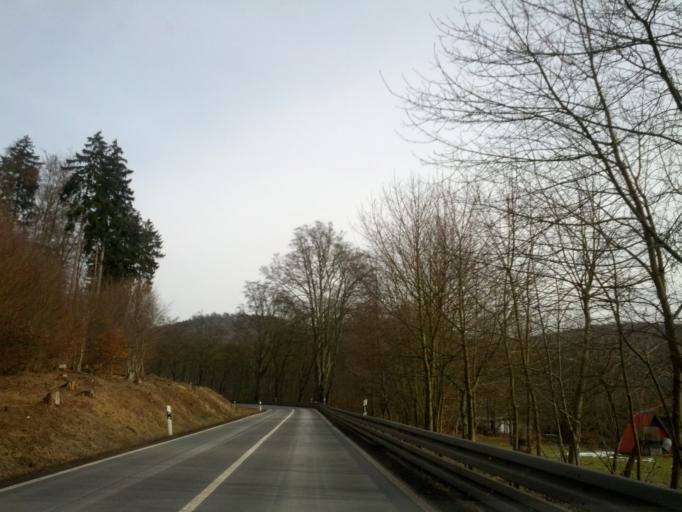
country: DE
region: Thuringia
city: Steinbach
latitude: 50.8440
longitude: 10.3632
